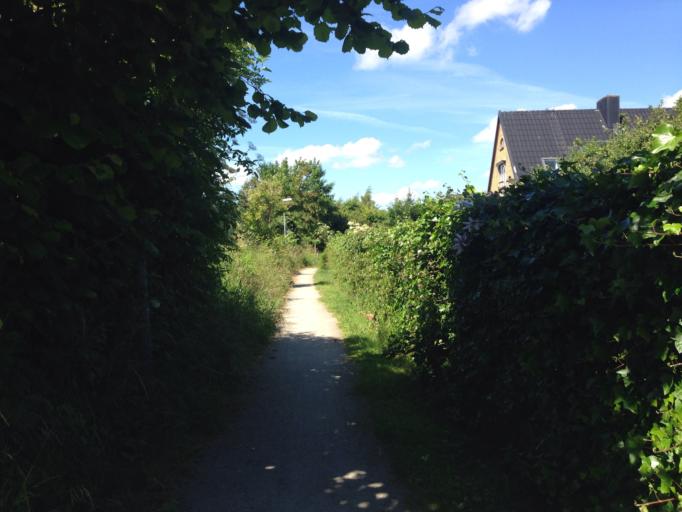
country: SE
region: Skane
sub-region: Lomma Kommun
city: Lomma
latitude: 55.6720
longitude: 13.0750
